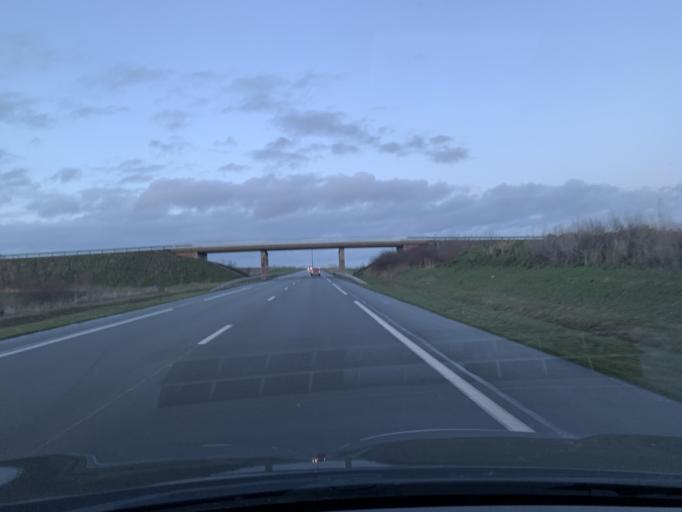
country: FR
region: Nord-Pas-de-Calais
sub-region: Departement du Nord
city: Escaudoeuvres
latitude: 50.1550
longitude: 3.2943
